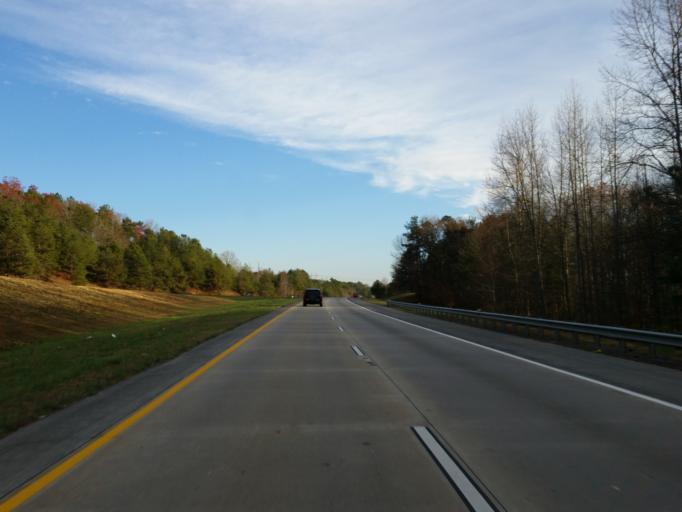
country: US
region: Georgia
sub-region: Cherokee County
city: Canton
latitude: 34.2851
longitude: -84.4460
